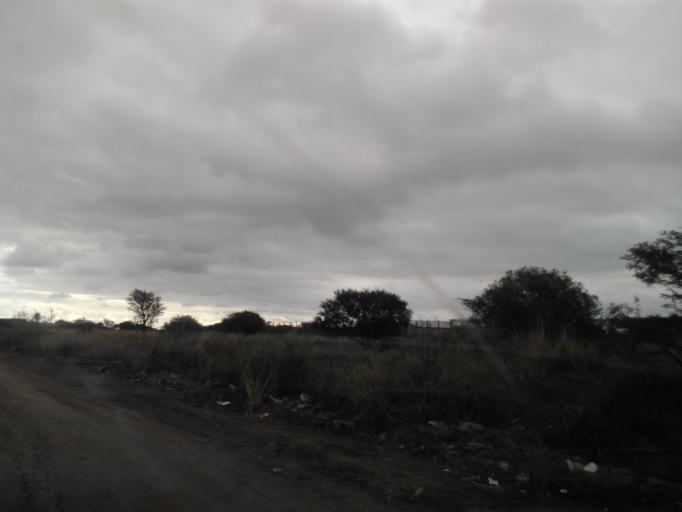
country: AR
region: Chaco
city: Fontana
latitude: -27.4582
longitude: -59.0419
